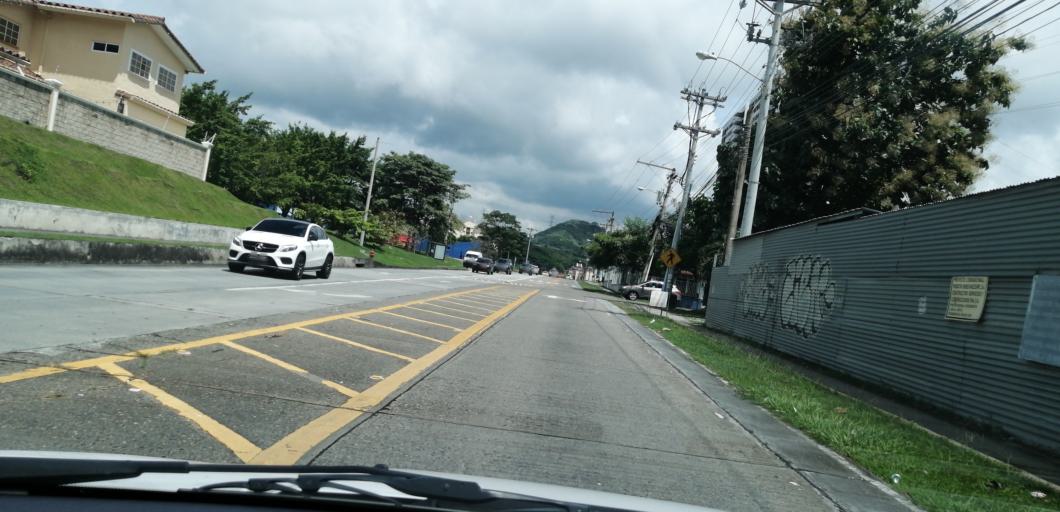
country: PA
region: Panama
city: Panama
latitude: 9.0332
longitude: -79.5272
